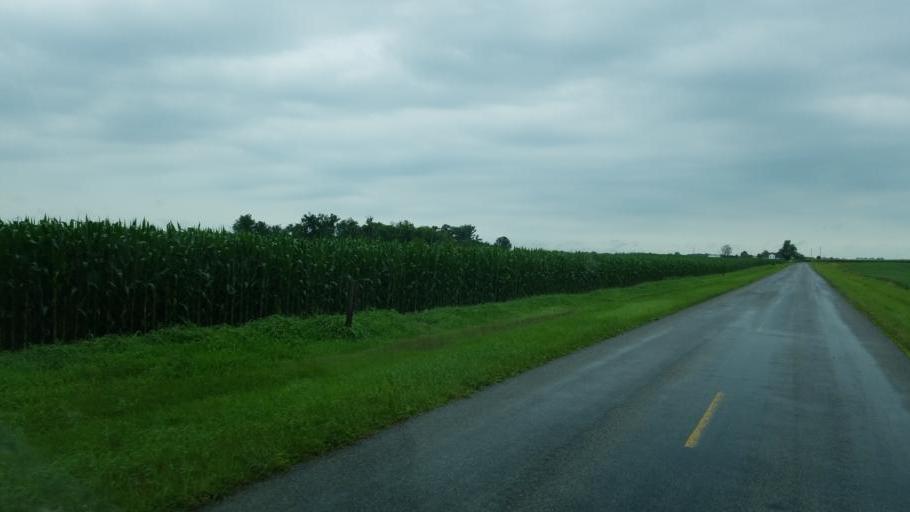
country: US
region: Ohio
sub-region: Union County
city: Richwood
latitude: 40.5150
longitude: -83.4456
